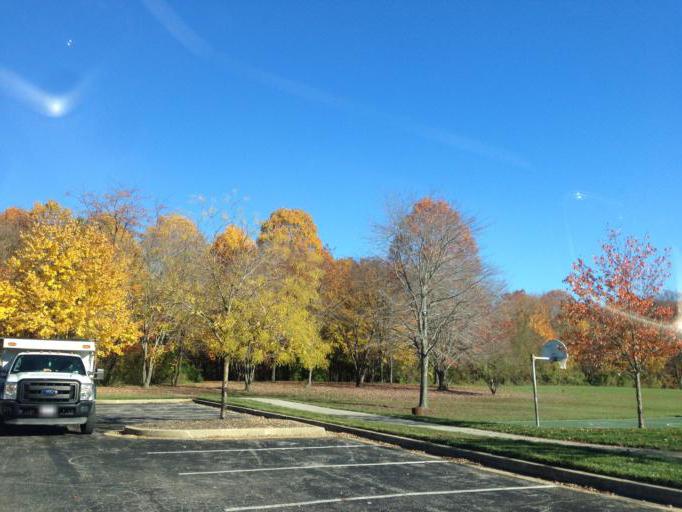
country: US
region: Maryland
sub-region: Howard County
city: Riverside
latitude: 39.2068
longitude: -76.8833
